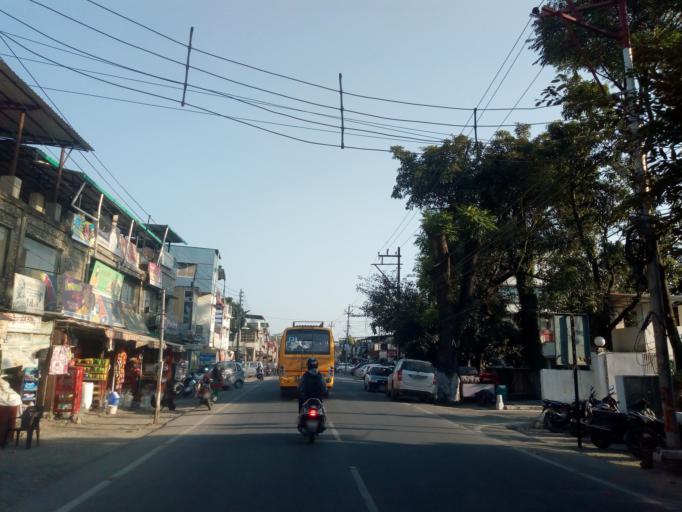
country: IN
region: Uttarakhand
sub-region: Dehradun
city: Dehradun
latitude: 30.3421
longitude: 78.0496
